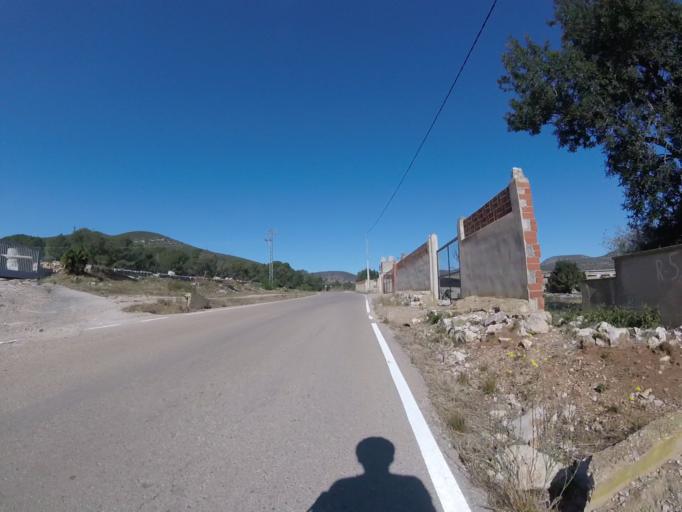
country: ES
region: Valencia
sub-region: Provincia de Castello
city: Santa Magdalena de Pulpis
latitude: 40.3638
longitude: 0.2796
